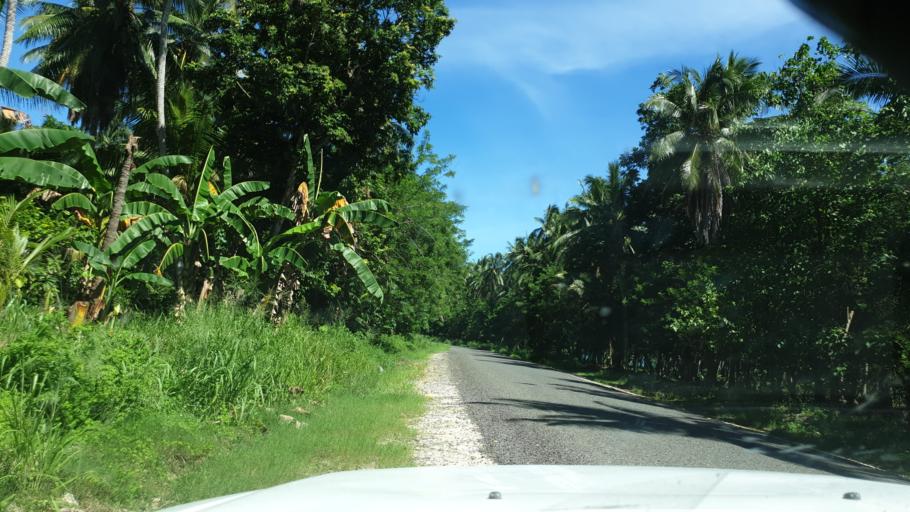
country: PG
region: Madang
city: Madang
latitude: -4.5064
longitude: 145.4614
